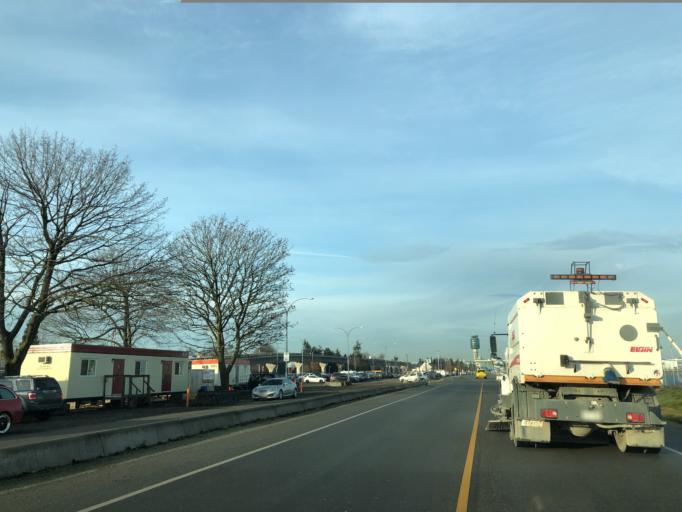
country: CA
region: British Columbia
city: Richmond
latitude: 49.1934
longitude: -123.1637
